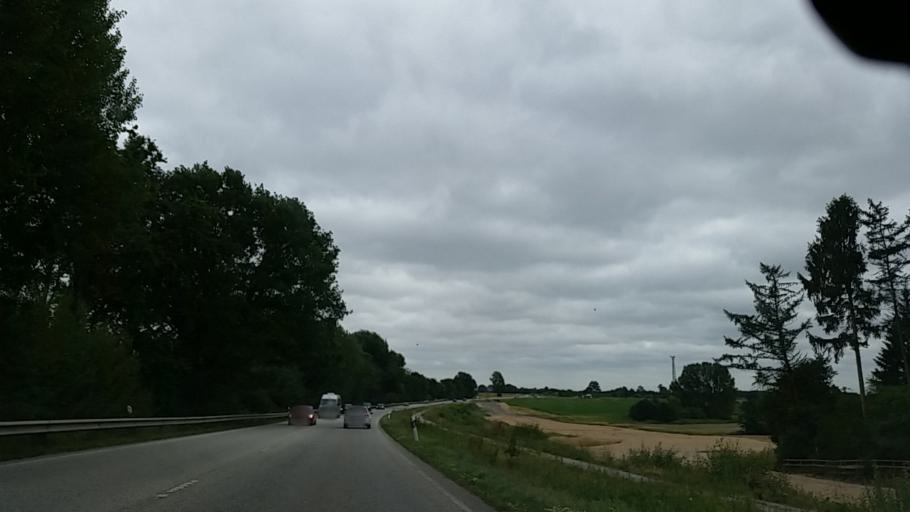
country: DE
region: Schleswig-Holstein
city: Loptin
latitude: 54.1791
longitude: 10.2013
